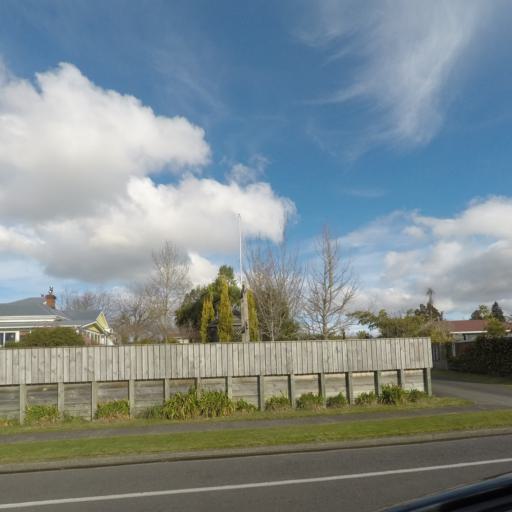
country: NZ
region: Manawatu-Wanganui
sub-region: Ruapehu District
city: Waiouru
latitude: -39.4142
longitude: 175.4025
